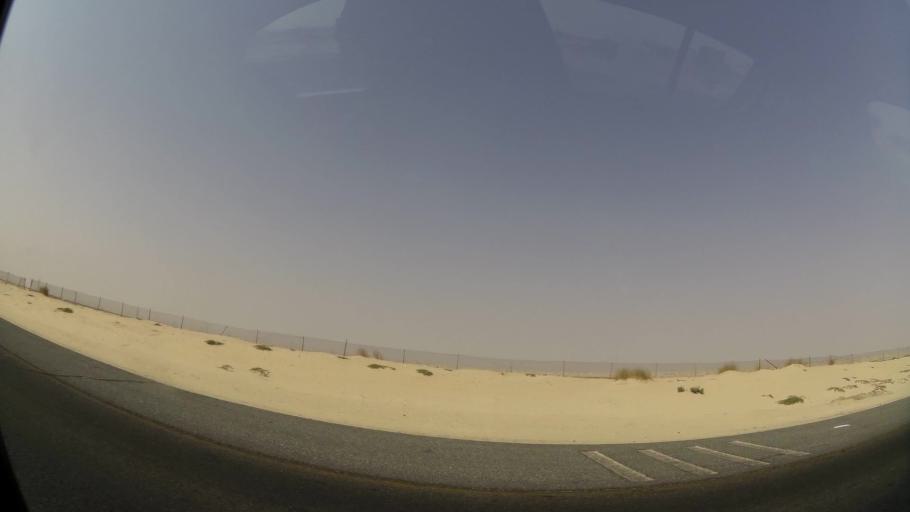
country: KW
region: Muhafazat al Jahra'
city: Al Jahra'
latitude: 29.3542
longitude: 47.6329
